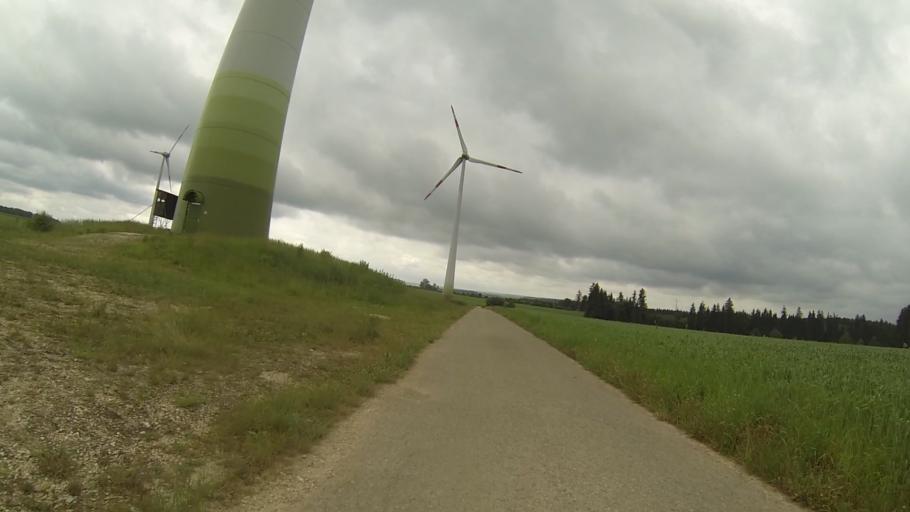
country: DE
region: Baden-Wuerttemberg
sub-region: Regierungsbezirk Stuttgart
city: Bartholoma
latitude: 48.6933
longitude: 9.9932
